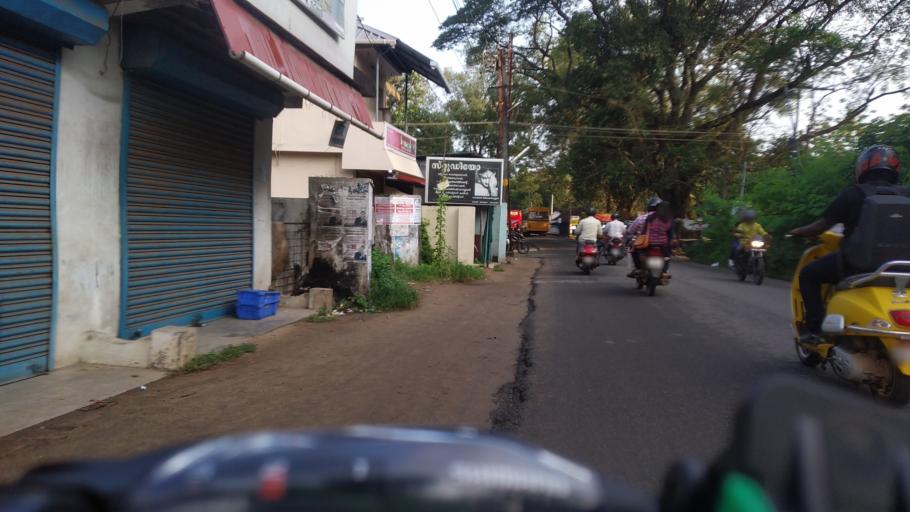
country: IN
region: Kerala
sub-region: Ernakulam
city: Elur
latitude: 10.0726
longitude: 76.2118
